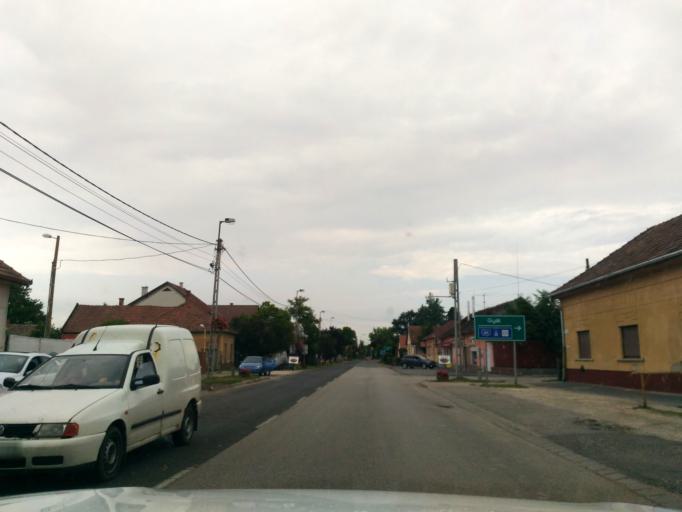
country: HU
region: Pest
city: Alsonemedi
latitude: 47.3133
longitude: 19.1669
